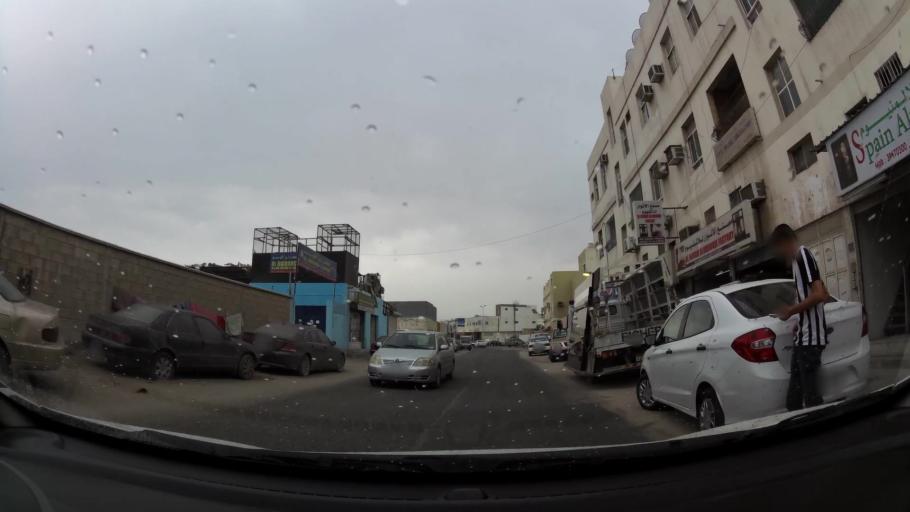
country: BH
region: Northern
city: Madinat `Isa
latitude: 26.1839
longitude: 50.5272
